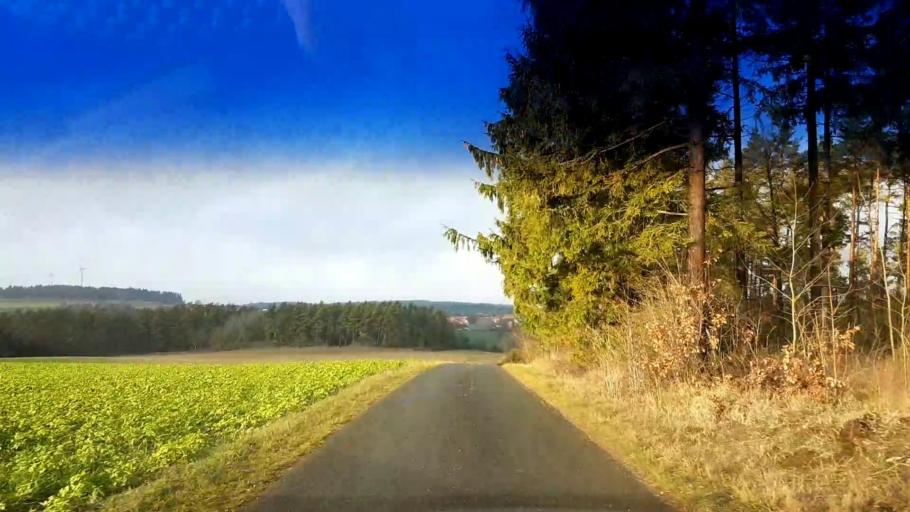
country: DE
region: Bavaria
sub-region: Upper Franconia
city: Poxdorf
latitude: 49.9248
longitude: 11.1257
